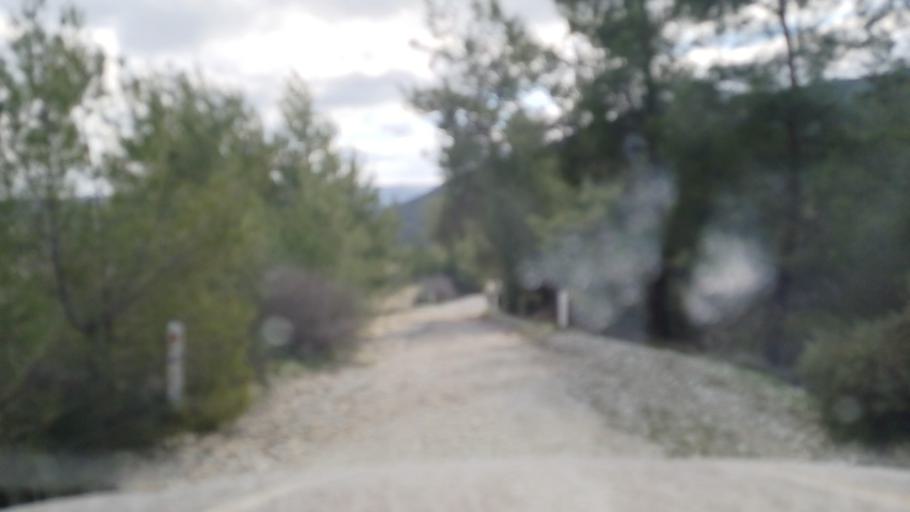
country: CY
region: Limassol
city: Pachna
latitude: 34.8407
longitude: 32.7138
